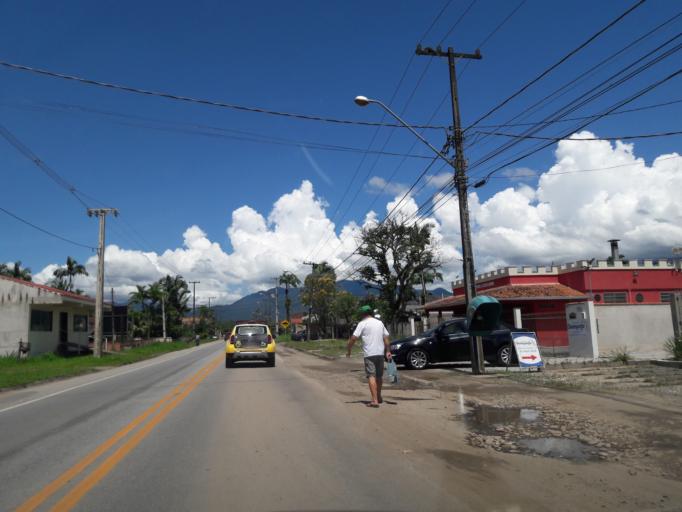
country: BR
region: Parana
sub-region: Antonina
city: Antonina
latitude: -25.4916
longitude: -48.8229
